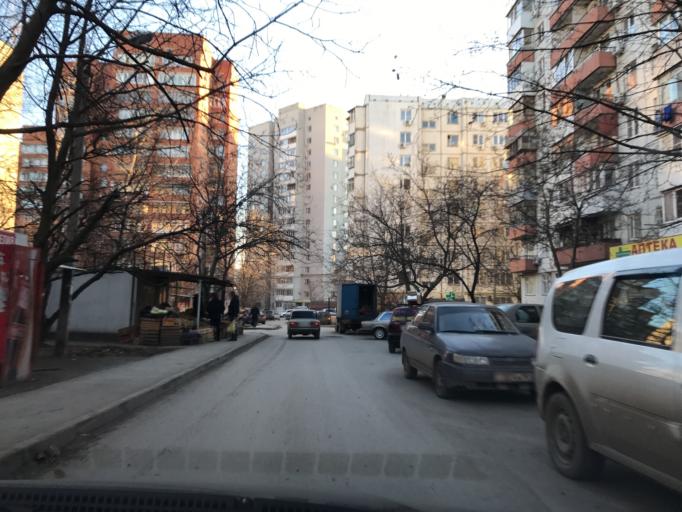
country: RU
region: Rostov
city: Rostov-na-Donu
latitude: 47.2309
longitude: 39.6195
